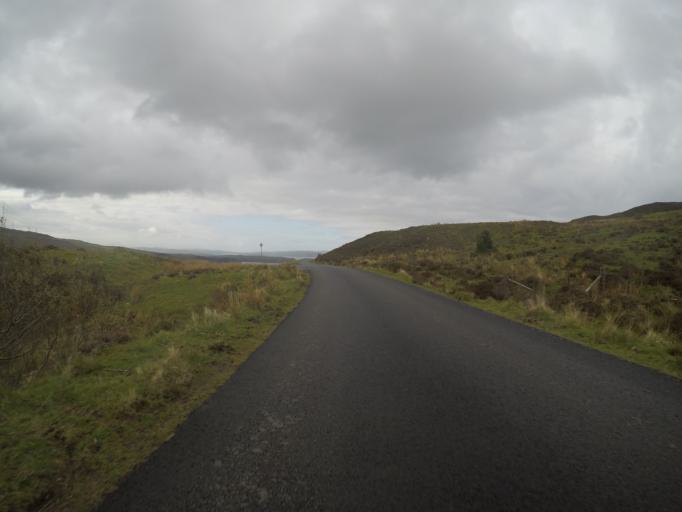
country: GB
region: Scotland
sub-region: Highland
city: Portree
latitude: 57.5968
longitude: -6.3579
